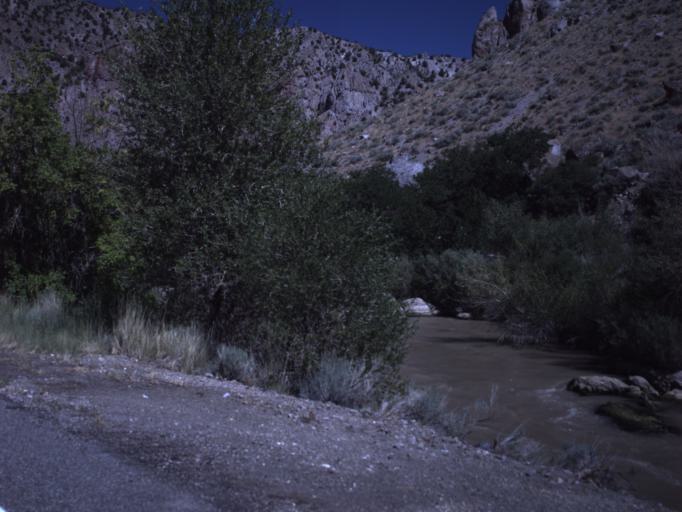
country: US
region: Utah
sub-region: Sevier County
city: Monroe
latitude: 38.5691
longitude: -112.2634
